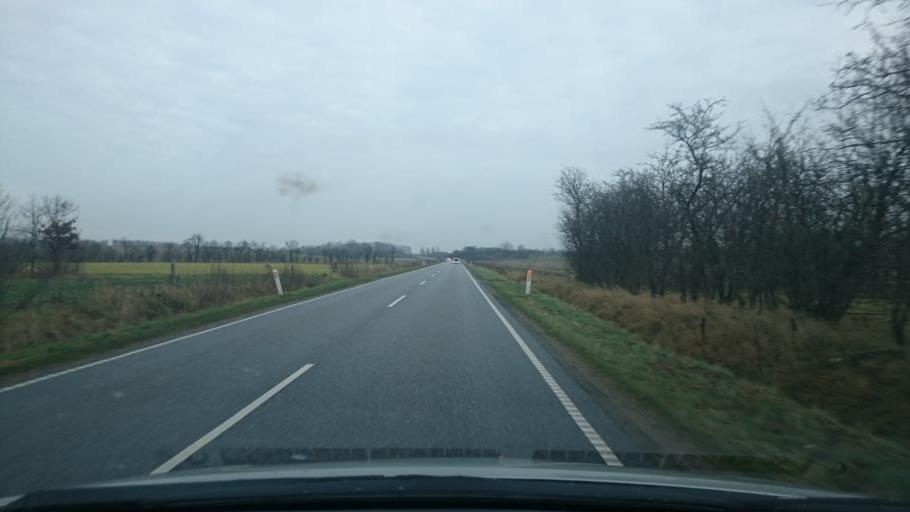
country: DK
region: South Denmark
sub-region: Esbjerg Kommune
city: Ribe
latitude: 55.3330
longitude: 8.9123
